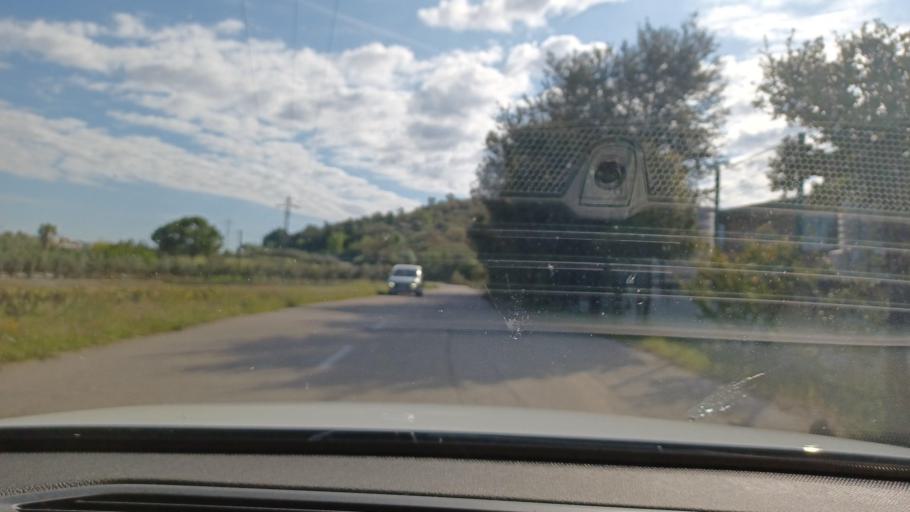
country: ES
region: Catalonia
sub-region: Provincia de Barcelona
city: Vilafranca del Penedes
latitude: 41.3616
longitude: 1.6757
